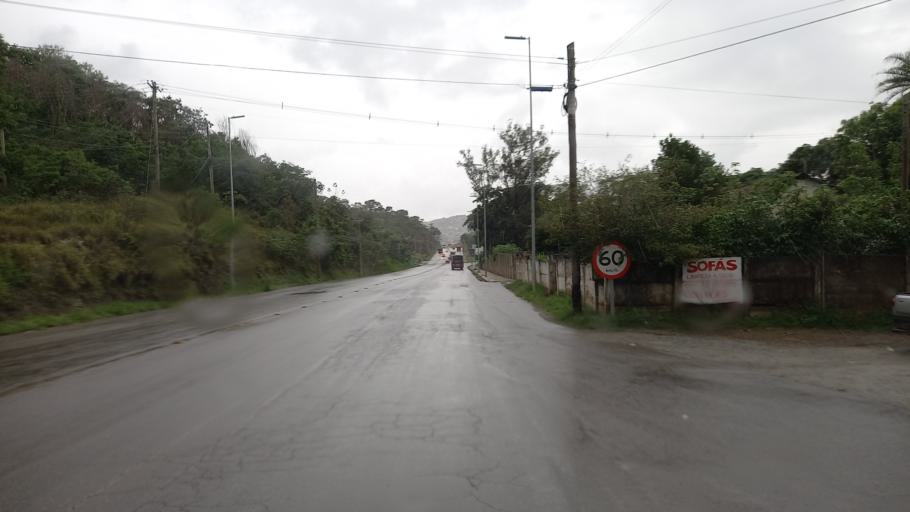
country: BR
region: Minas Gerais
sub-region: Belo Horizonte
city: Belo Horizonte
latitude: -19.8758
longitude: -43.8731
